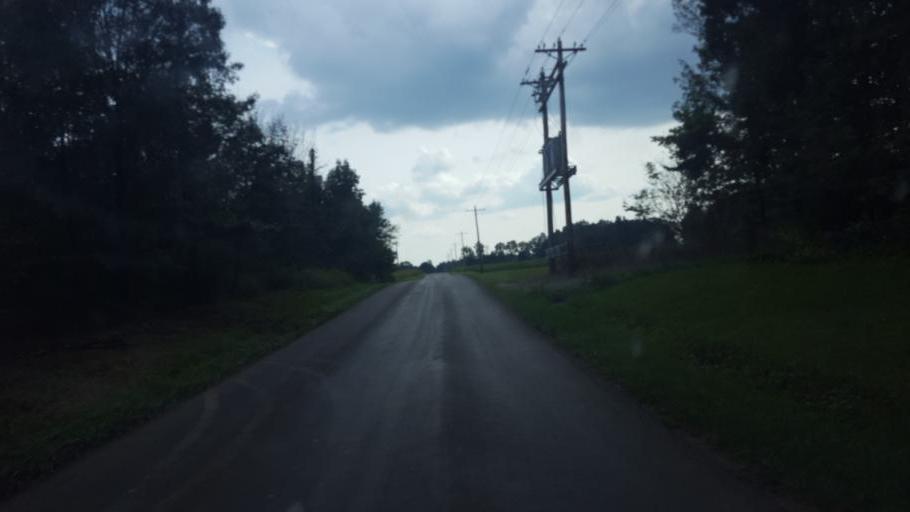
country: US
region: Ohio
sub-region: Knox County
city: Gambier
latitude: 40.3696
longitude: -82.3538
